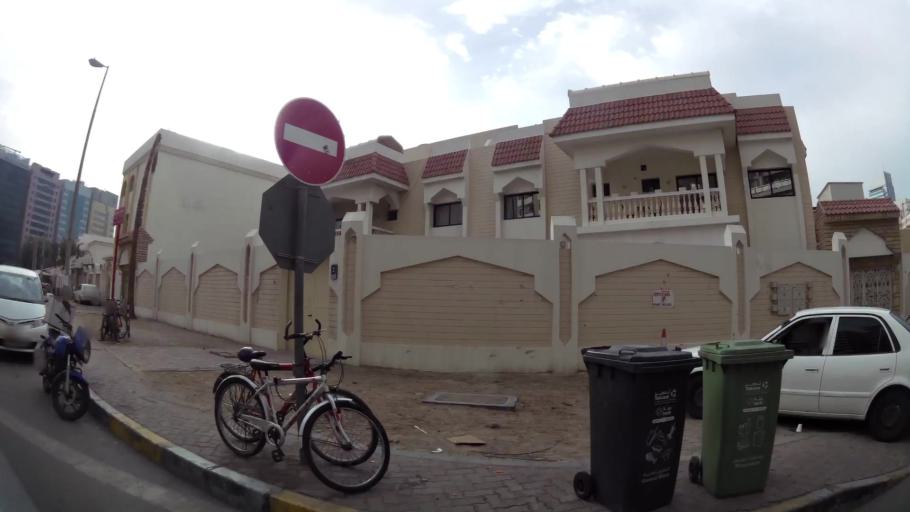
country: AE
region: Abu Dhabi
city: Abu Dhabi
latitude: 24.4771
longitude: 54.3688
